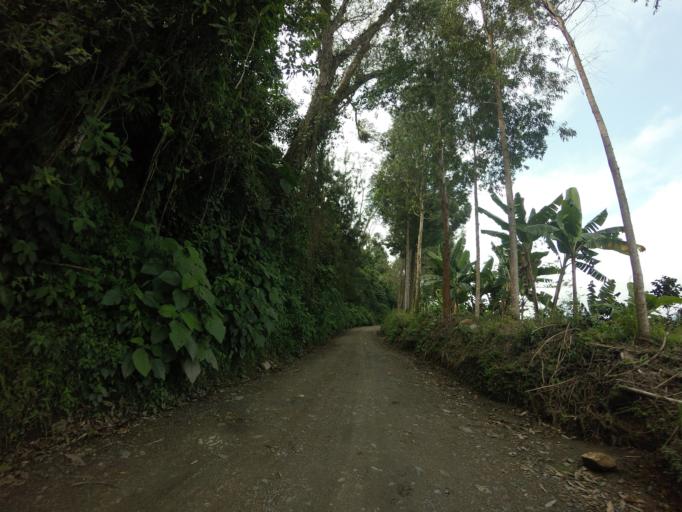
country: CO
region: Caldas
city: Marquetalia
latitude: 5.3508
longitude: -75.0559
